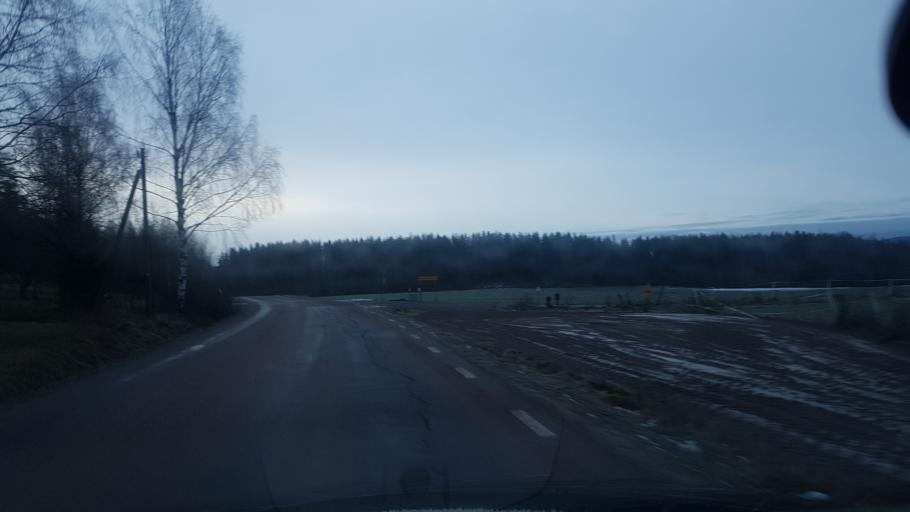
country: SE
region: Dalarna
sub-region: Borlange Kommun
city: Ornas
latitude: 60.4408
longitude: 15.6462
